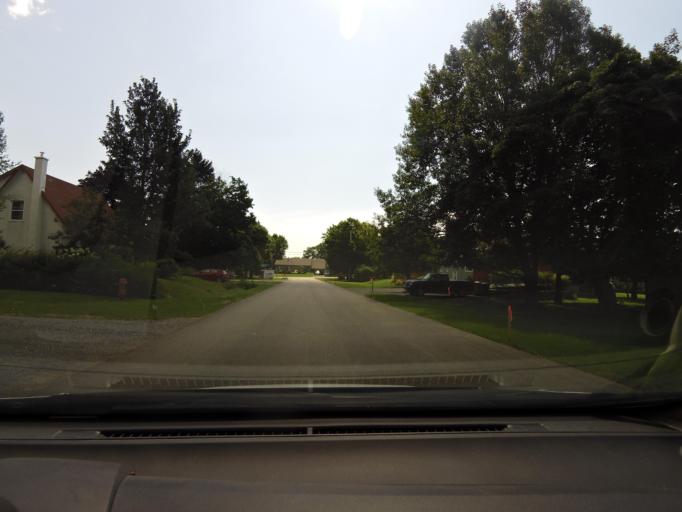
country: CA
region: Quebec
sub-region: Capitale-Nationale
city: Neuville
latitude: 46.7165
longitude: -71.5435
